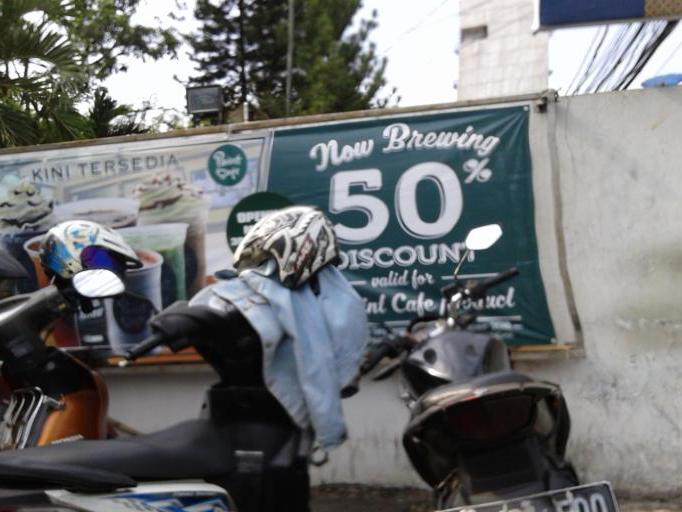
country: ID
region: West Java
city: Pamulang
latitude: -6.2963
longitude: 106.7949
